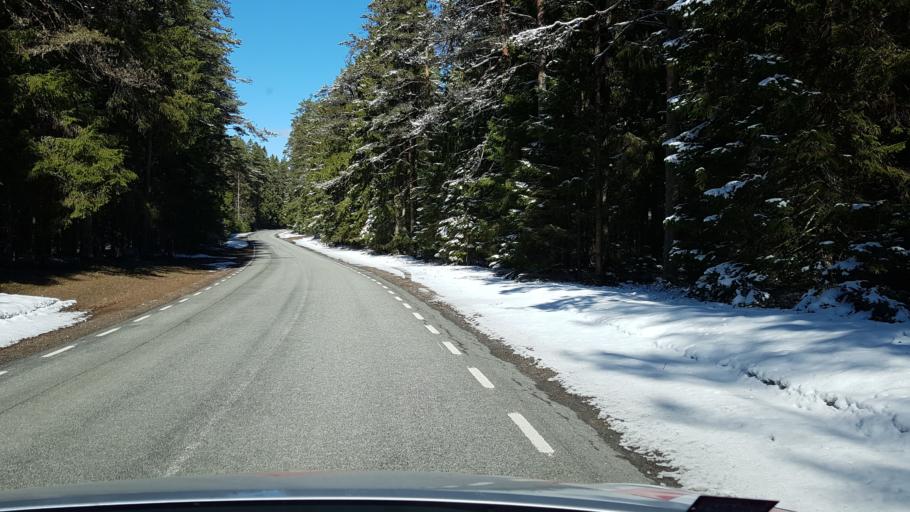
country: EE
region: Laeaene-Virumaa
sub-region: Kadrina vald
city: Kadrina
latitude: 59.4428
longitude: 26.0152
